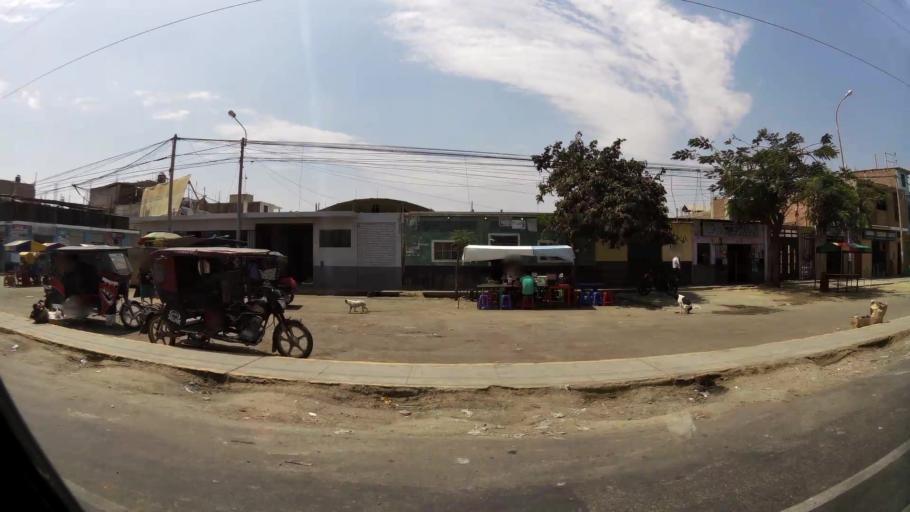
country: PE
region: La Libertad
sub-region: Chepen
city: Pacanga
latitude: -7.1570
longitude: -79.4431
